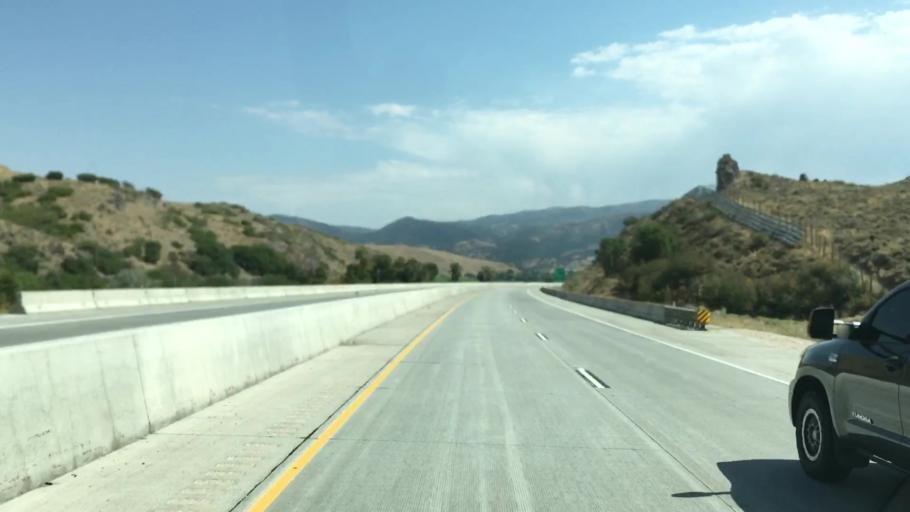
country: US
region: Utah
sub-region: Summit County
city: Coalville
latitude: 40.8061
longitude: -111.4328
